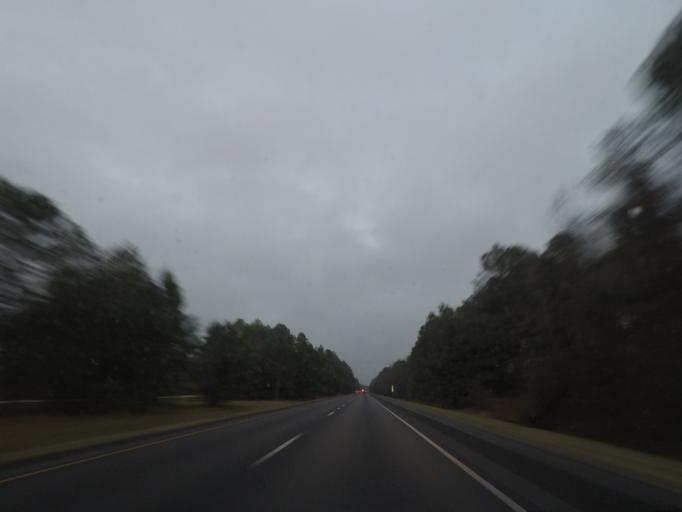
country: US
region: South Carolina
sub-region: Clarendon County
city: Manning
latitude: 33.7838
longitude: -80.1688
